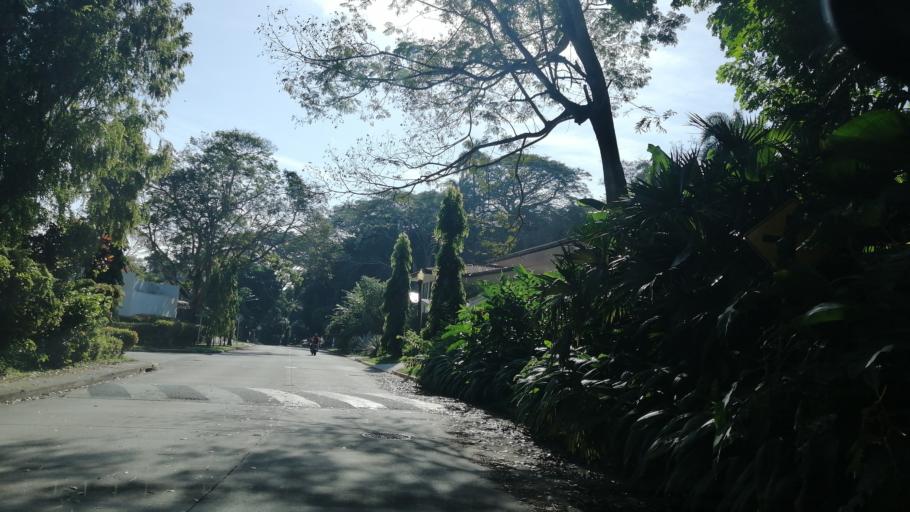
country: PA
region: Panama
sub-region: Distrito de Panama
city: Ancon
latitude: 8.9627
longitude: -79.5473
